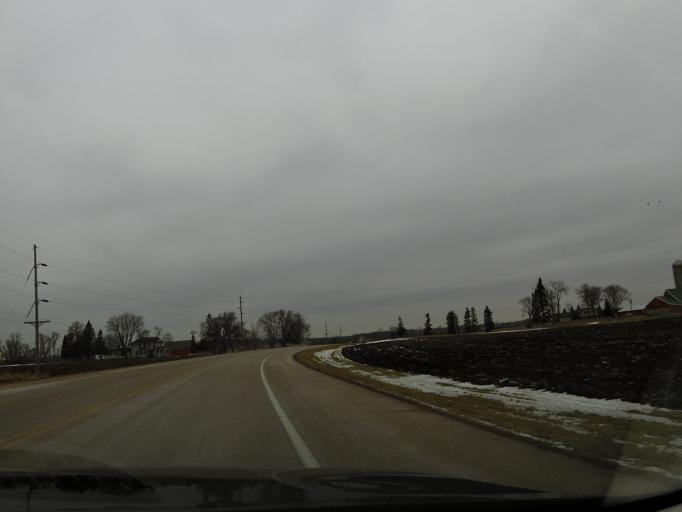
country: US
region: Minnesota
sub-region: Carver County
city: Watertown
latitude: 44.9425
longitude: -93.8329
